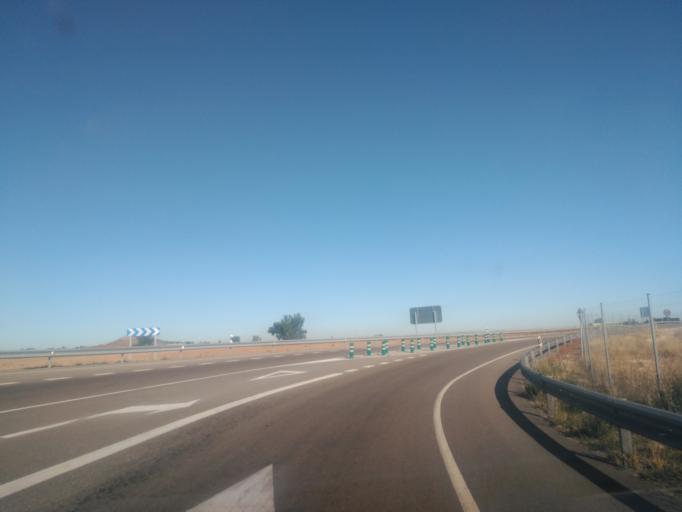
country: ES
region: Castille and Leon
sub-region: Provincia de Burgos
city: Castrillo de la Vega
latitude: 41.6372
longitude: -3.7815
